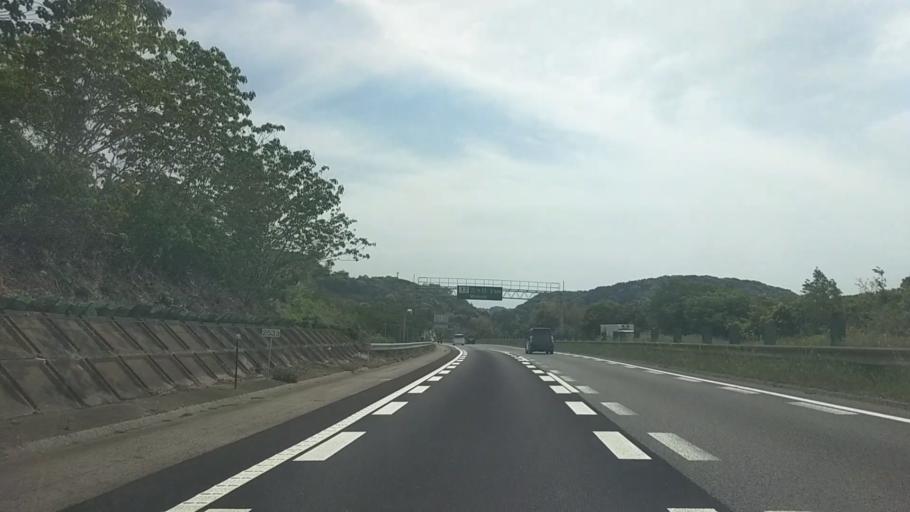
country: JP
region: Shizuoka
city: Kosai-shi
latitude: 34.8082
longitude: 137.5595
